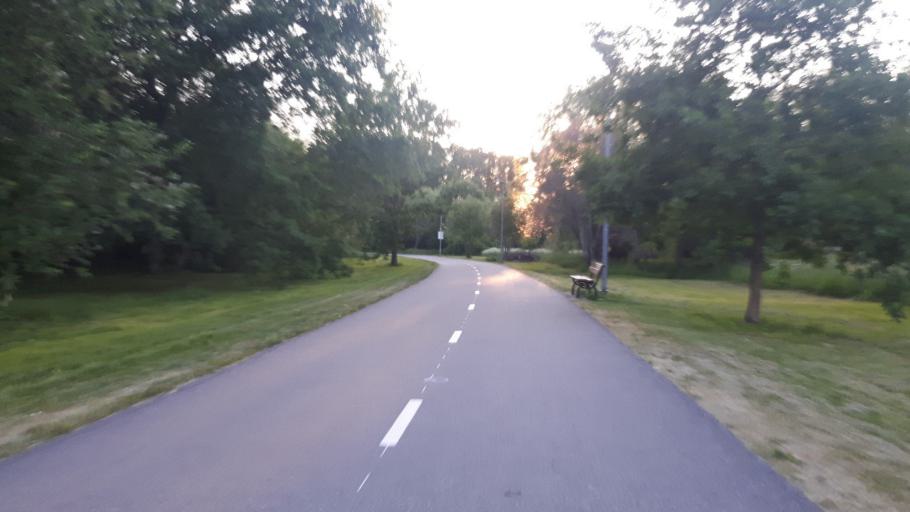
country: EE
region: Paernumaa
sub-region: Paernu linn
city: Parnu
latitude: 58.3703
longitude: 24.5307
